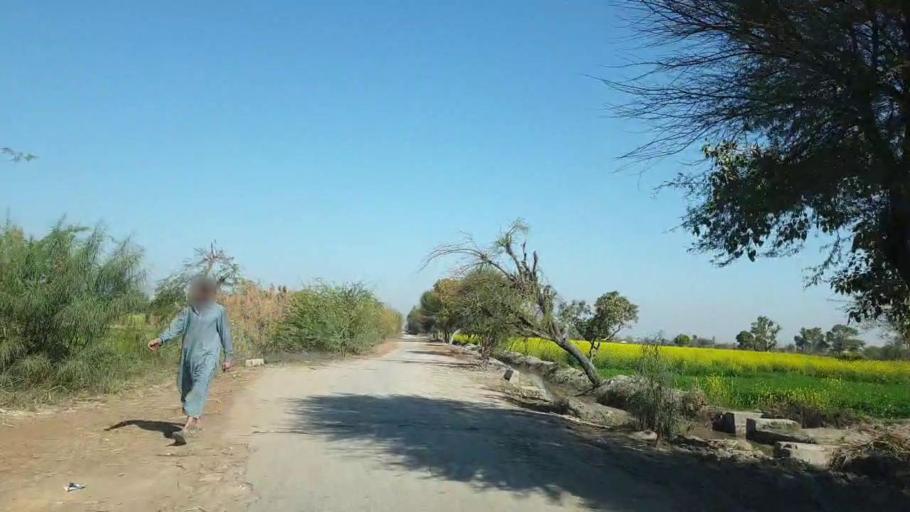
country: PK
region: Sindh
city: Mirpur Khas
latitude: 25.6122
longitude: 69.0242
